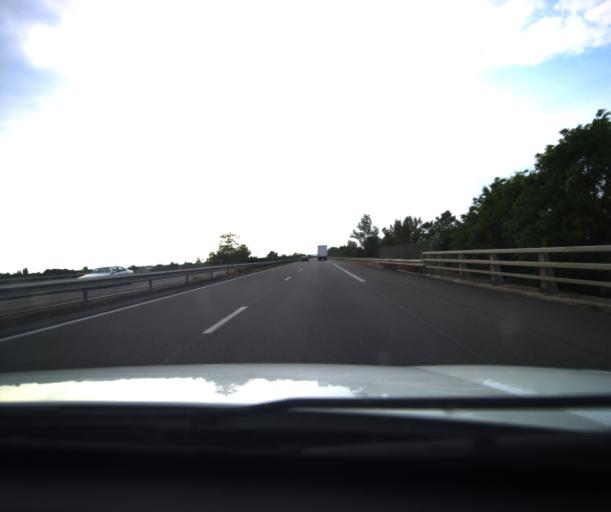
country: FR
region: Midi-Pyrenees
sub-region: Departement du Tarn-et-Garonne
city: Saint-Porquier
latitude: 44.0369
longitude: 1.1551
